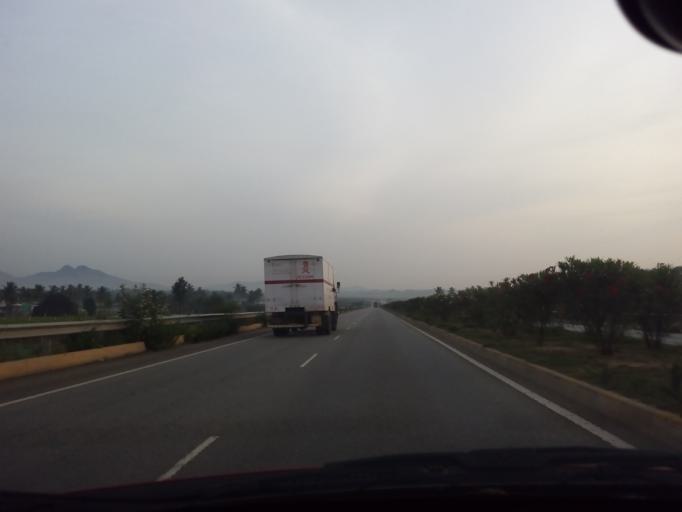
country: IN
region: Karnataka
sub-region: Chikkaballapur
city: Chik Ballapur
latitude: 13.4128
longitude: 77.7435
